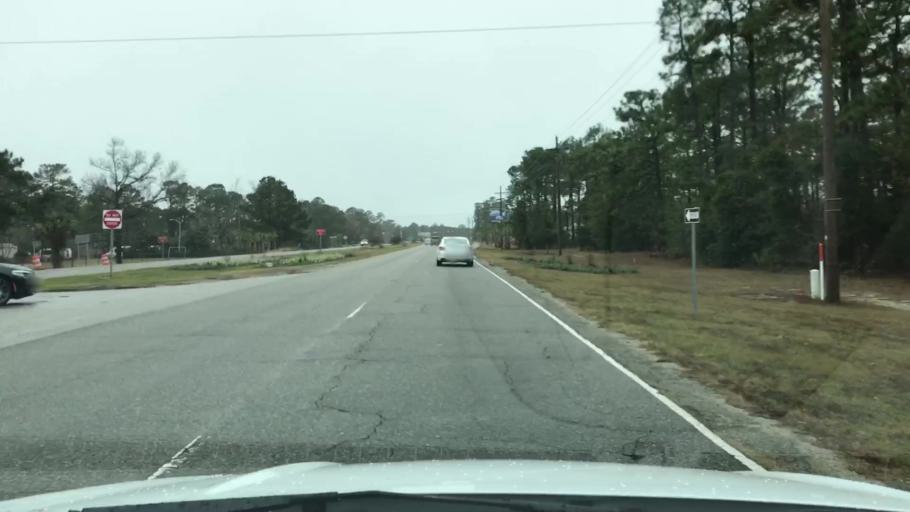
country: US
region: South Carolina
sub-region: Horry County
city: Myrtle Beach
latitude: 33.7473
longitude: -78.8362
